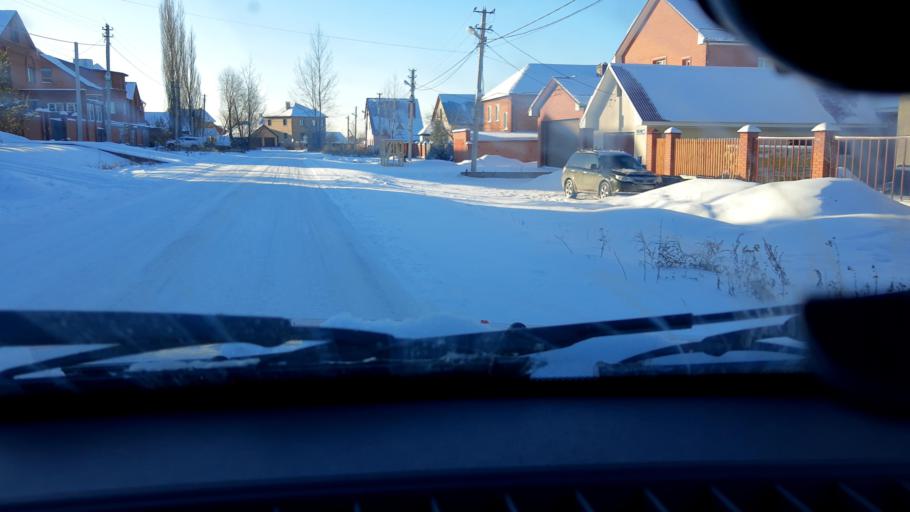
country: RU
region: Bashkortostan
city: Ufa
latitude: 54.6023
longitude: 55.9414
